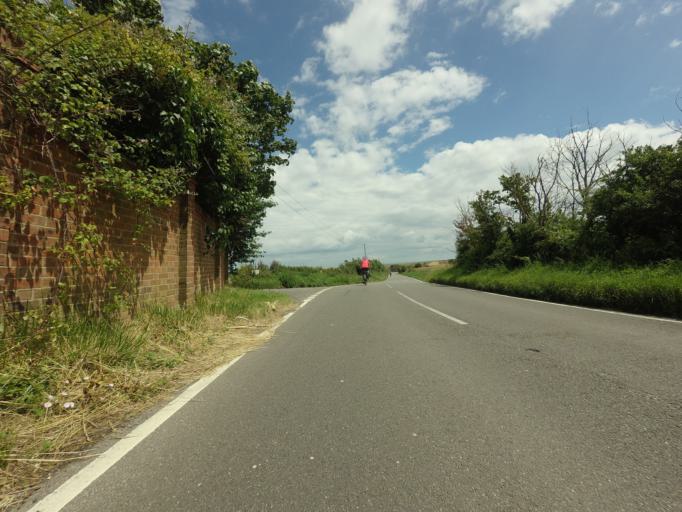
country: GB
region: England
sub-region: Medway
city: Allhallows
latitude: 51.4683
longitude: 0.6376
